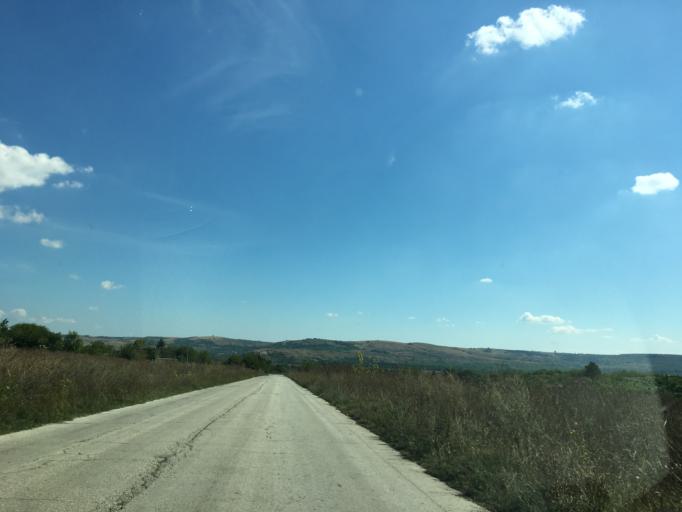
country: RO
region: Olt
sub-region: Comuna Orlea
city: Orlea
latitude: 43.6392
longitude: 24.3864
